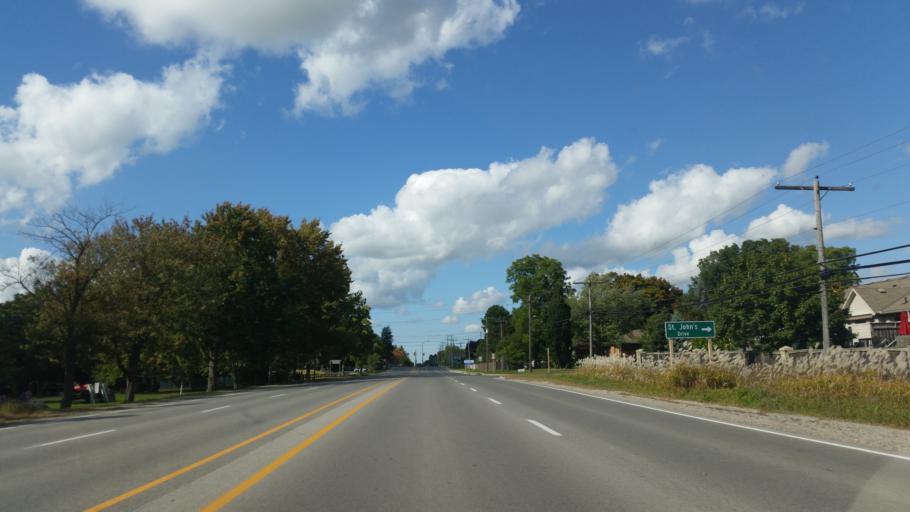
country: CA
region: Ontario
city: London
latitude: 43.0477
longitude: -81.2935
